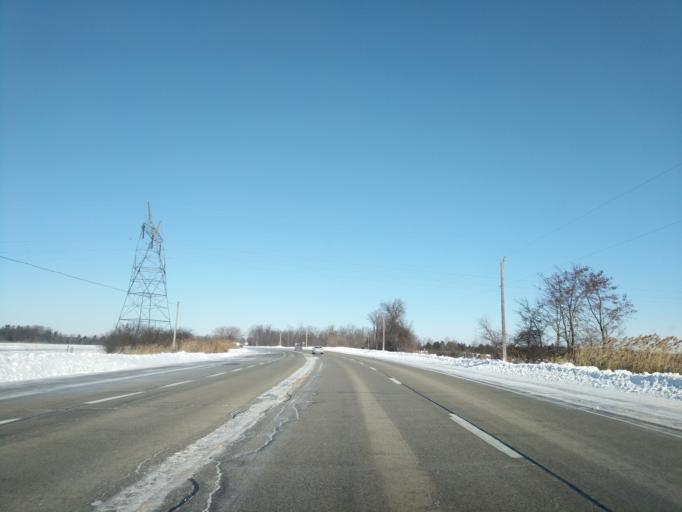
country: CA
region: Ontario
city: Pickering
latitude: 43.8655
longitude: -79.1354
